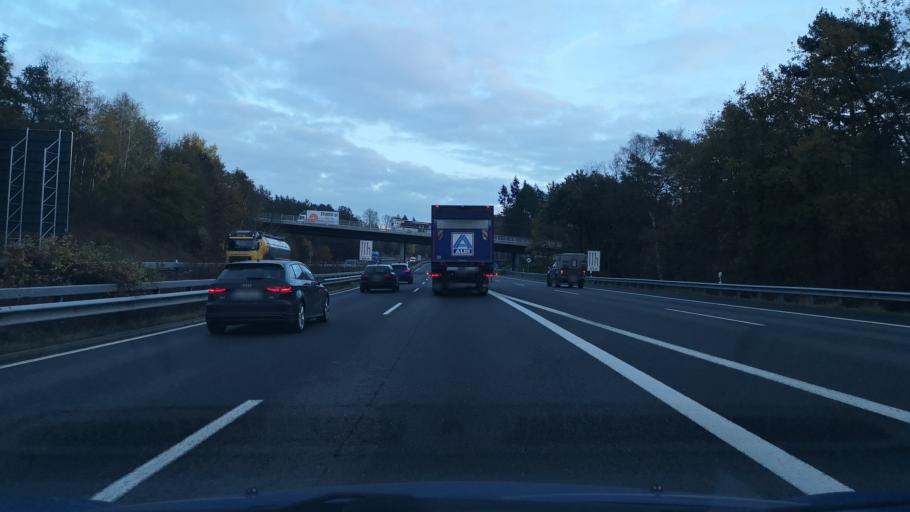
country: DE
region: Lower Saxony
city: Harmstorf
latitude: 53.3709
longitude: 10.0251
